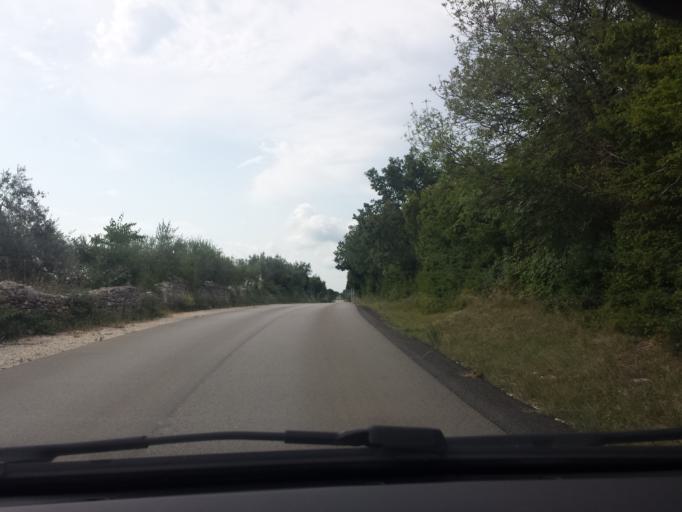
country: HR
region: Istarska
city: Galizana
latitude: 44.9413
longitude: 13.8667
